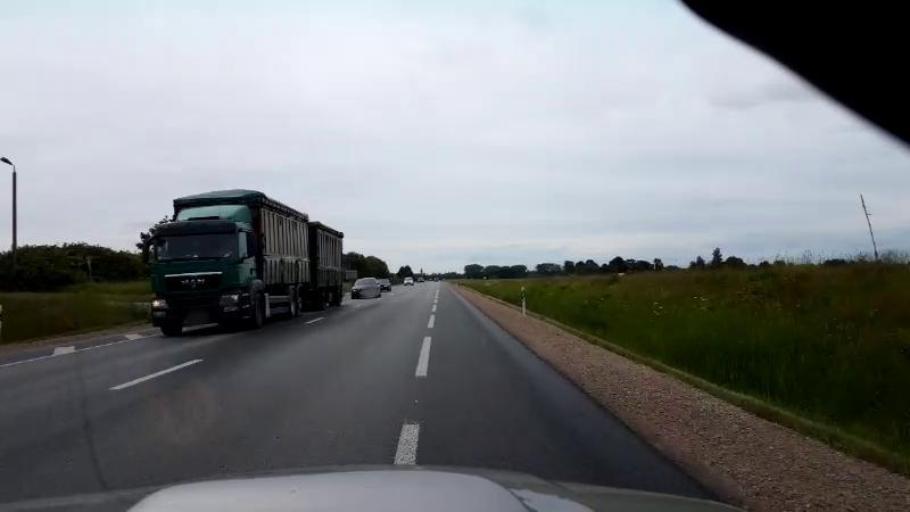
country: LV
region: Lecava
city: Iecava
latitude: 56.6170
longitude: 24.2168
